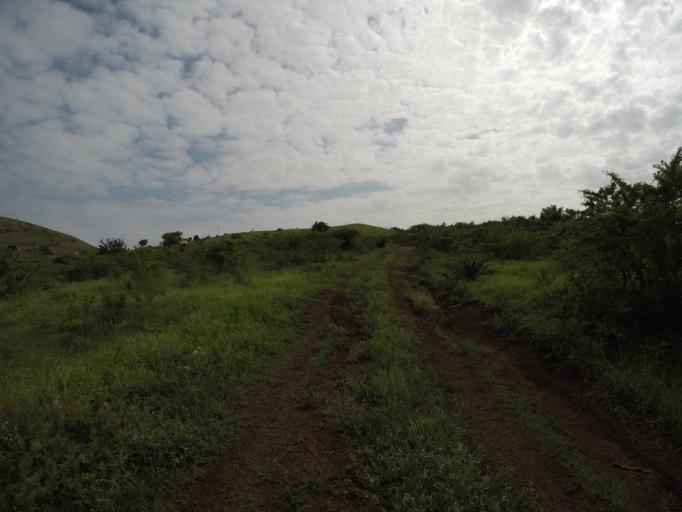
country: ZA
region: KwaZulu-Natal
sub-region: uThungulu District Municipality
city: Empangeni
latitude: -28.6224
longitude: 31.8947
